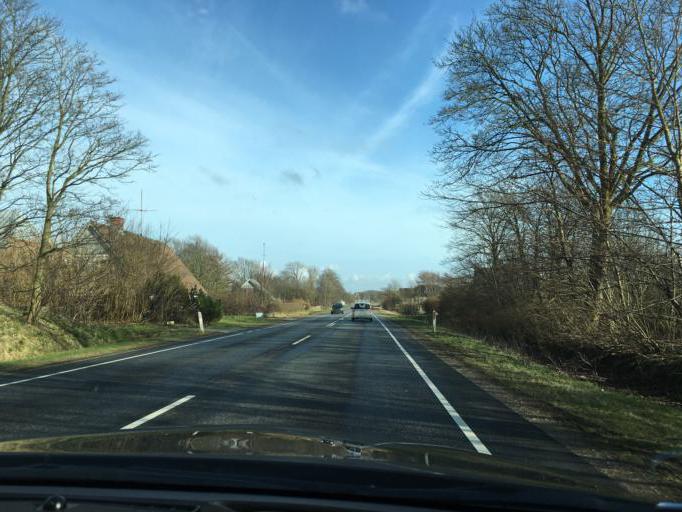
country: DK
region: South Denmark
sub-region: Esbjerg Kommune
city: Tjaereborg
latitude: 55.4920
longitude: 8.6292
